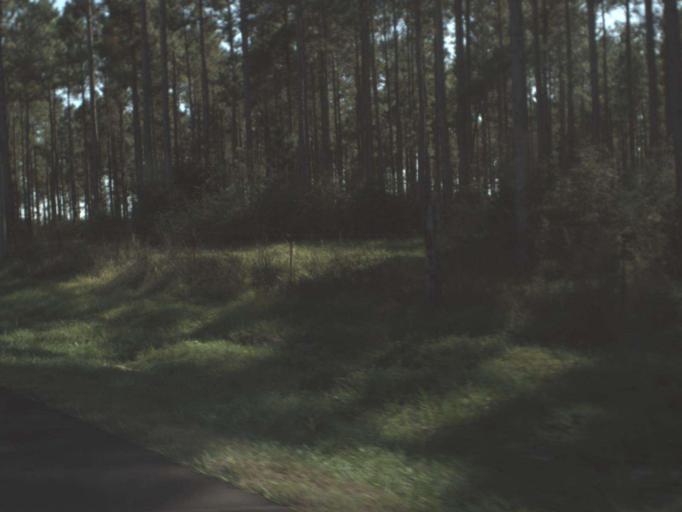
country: US
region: Florida
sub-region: Walton County
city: DeFuniak Springs
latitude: 30.8423
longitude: -86.2386
